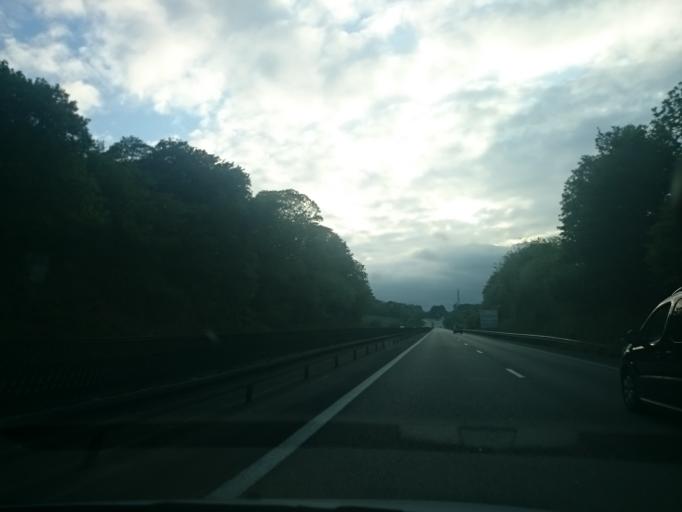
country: FR
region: Brittany
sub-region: Departement du Finistere
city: Quimperle
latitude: 47.8605
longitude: -3.5382
